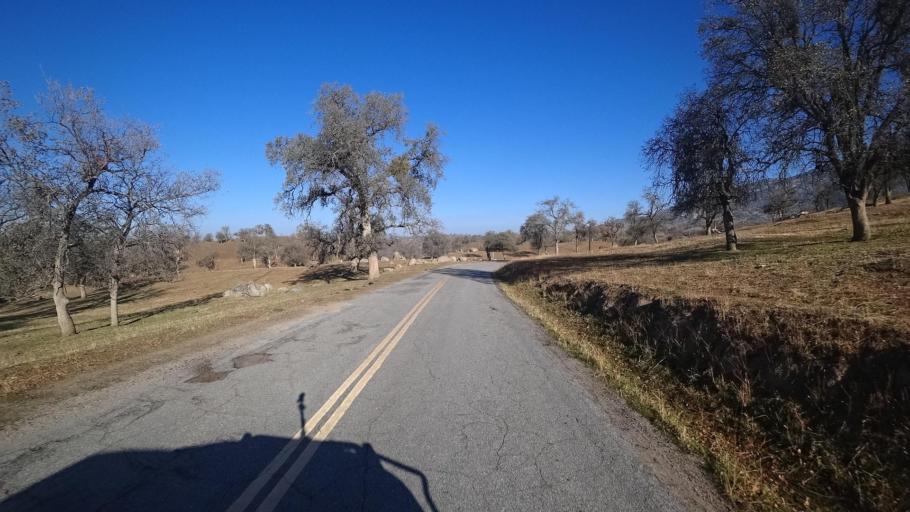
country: US
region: California
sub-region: Kern County
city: Alta Sierra
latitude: 35.7412
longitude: -118.8192
